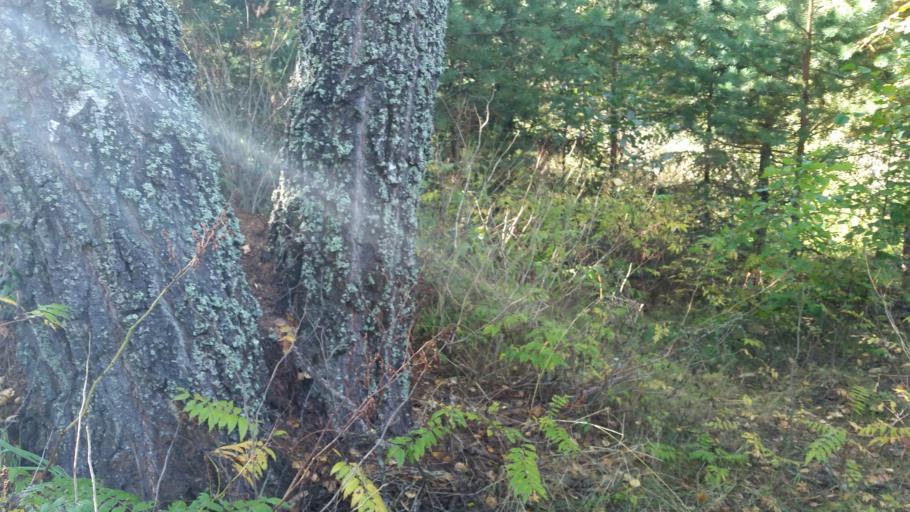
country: BY
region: Vitebsk
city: Vitebsk
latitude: 54.9763
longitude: 30.3405
